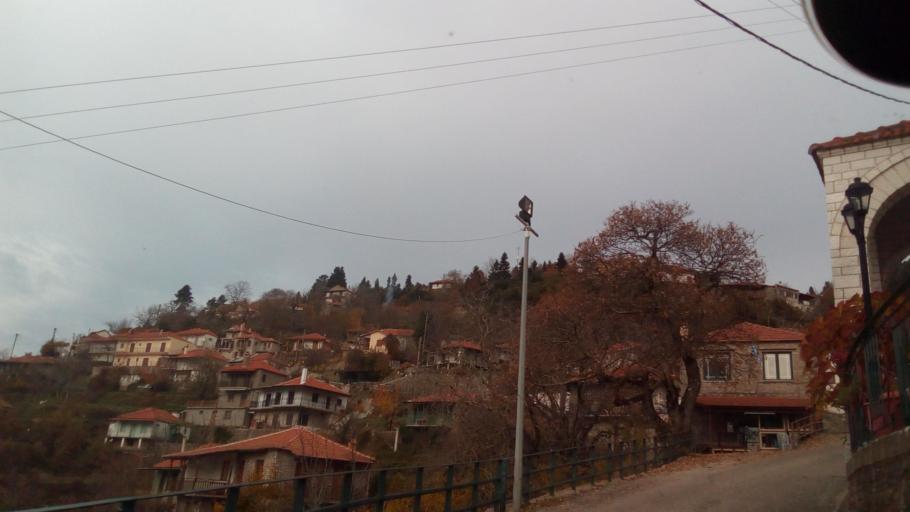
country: GR
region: West Greece
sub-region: Nomos Aitolias kai Akarnanias
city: Thermo
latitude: 38.6860
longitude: 21.8658
